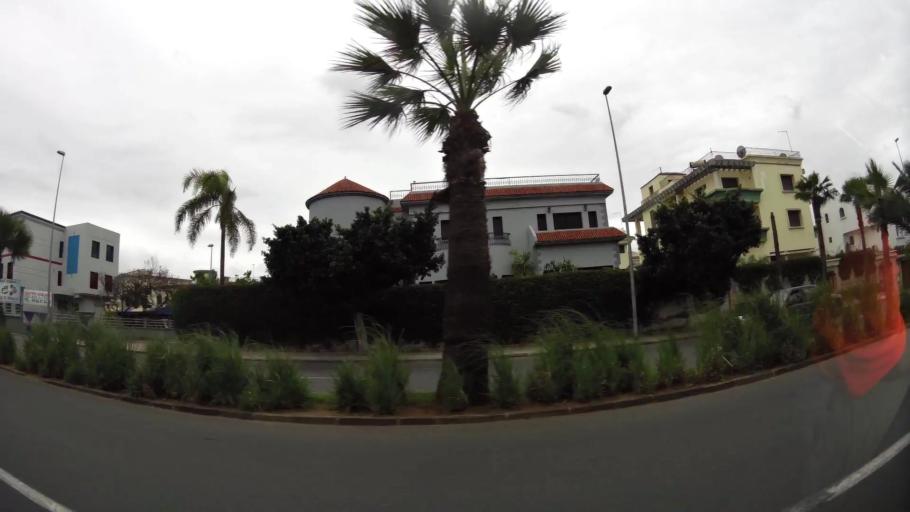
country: MA
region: Grand Casablanca
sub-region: Casablanca
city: Casablanca
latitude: 33.5616
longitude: -7.6236
